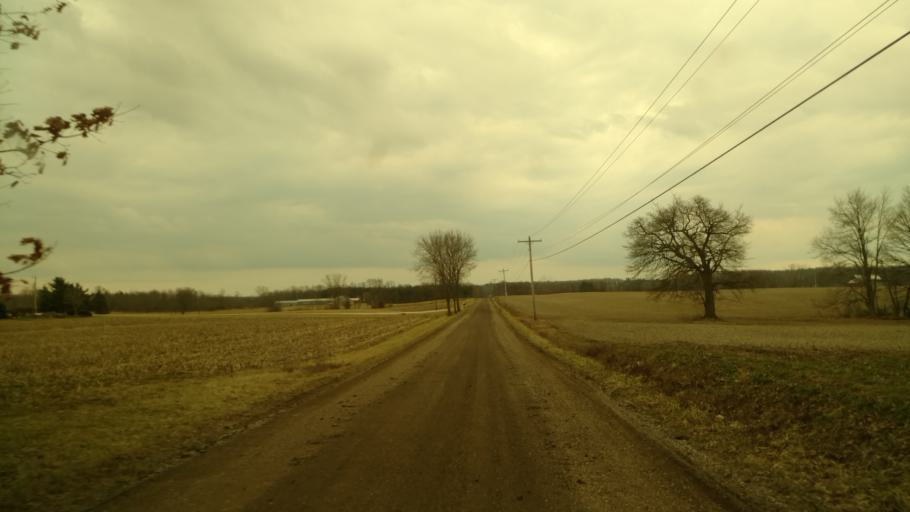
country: US
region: Ohio
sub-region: Richland County
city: Lexington
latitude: 40.6784
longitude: -82.6453
